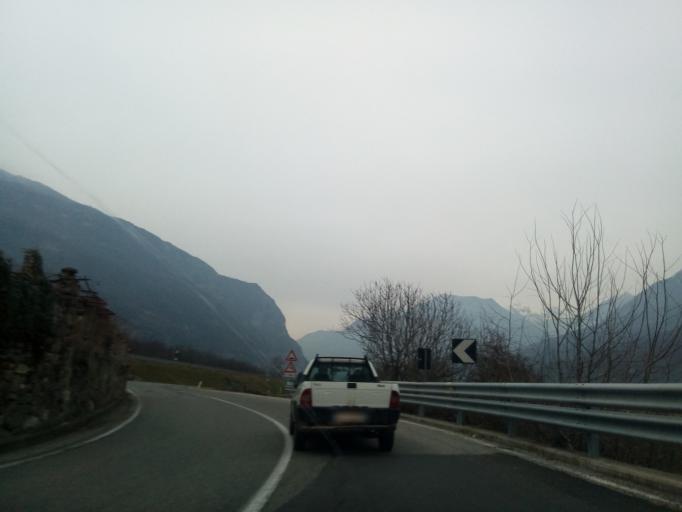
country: IT
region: Piedmont
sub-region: Provincia di Torino
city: Tavagnasco
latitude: 45.5500
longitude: 7.8229
